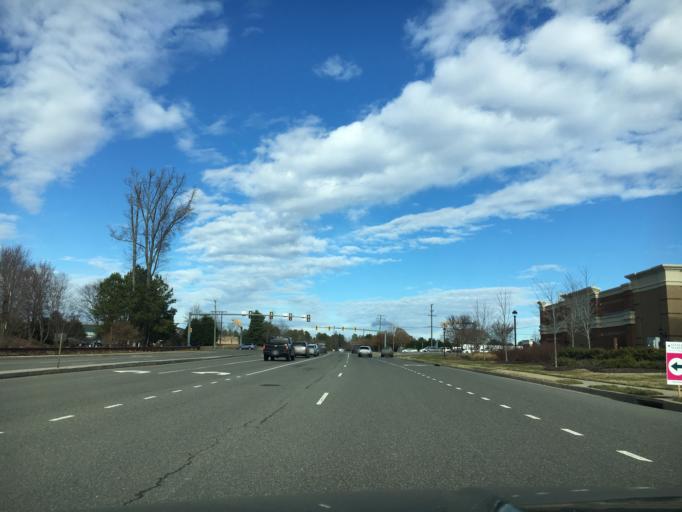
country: US
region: Virginia
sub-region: Henrico County
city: Short Pump
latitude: 37.6492
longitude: -77.6081
